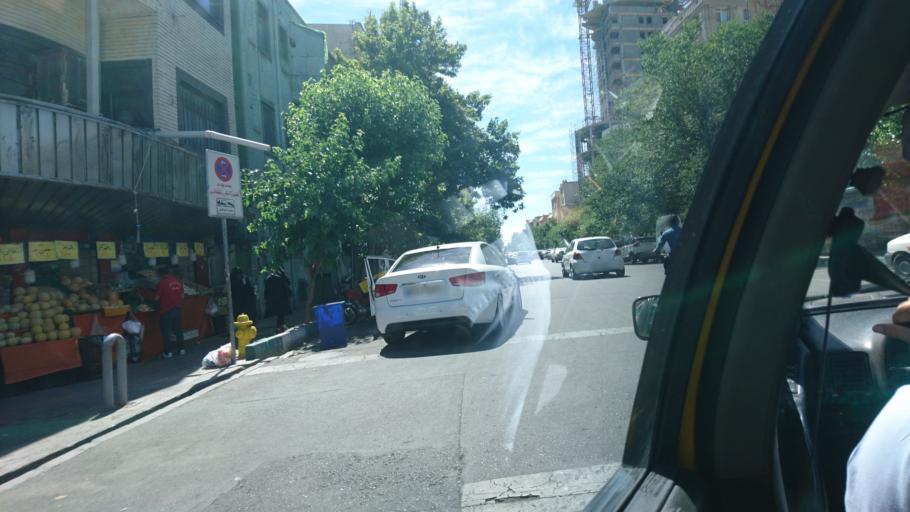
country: IR
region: Tehran
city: Tehran
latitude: 35.7014
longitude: 51.3913
